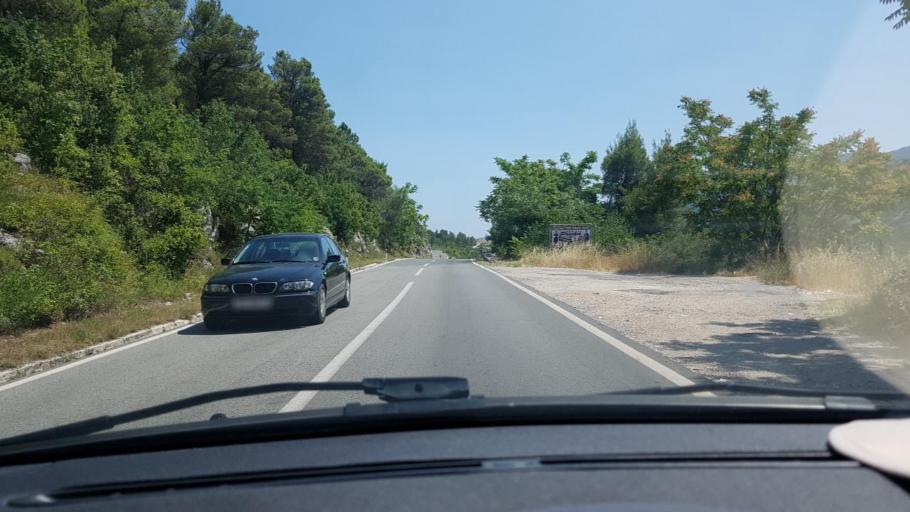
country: HR
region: Splitsko-Dalmatinska
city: Vrgorac
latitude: 43.1977
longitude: 17.3769
